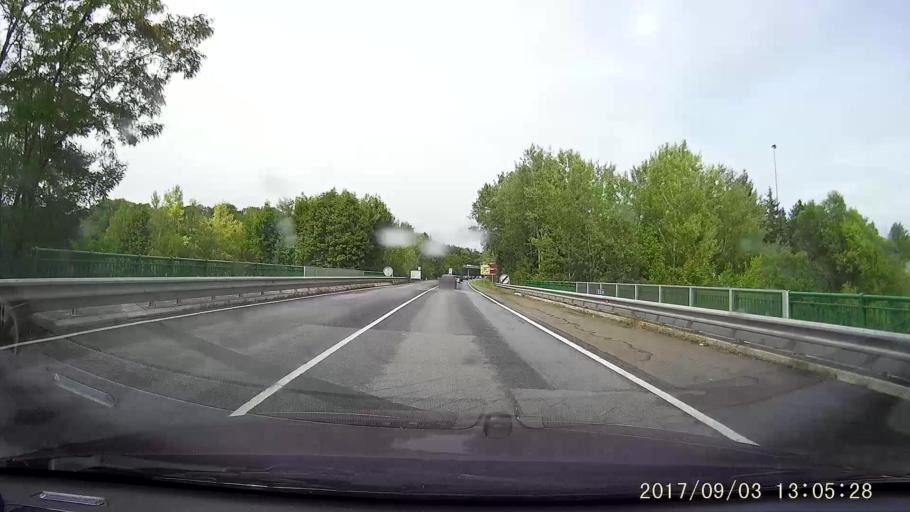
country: AT
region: Lower Austria
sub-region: Politischer Bezirk Hollabrunn
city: Hollabrunn
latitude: 48.5589
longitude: 16.0637
